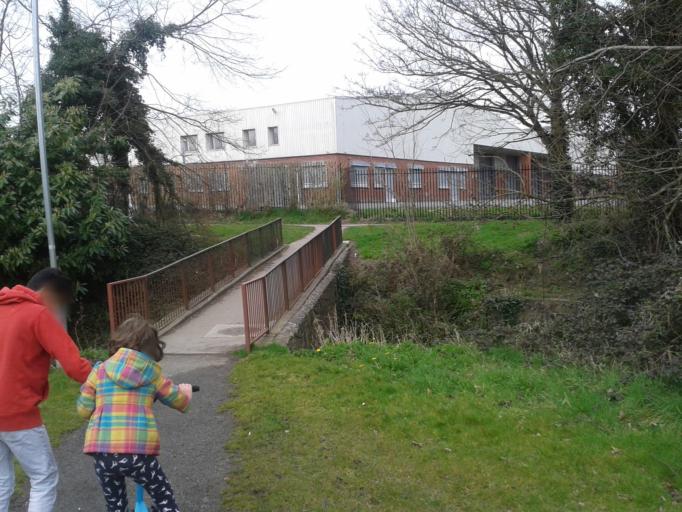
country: IE
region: Leinster
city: Beaumont
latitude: 53.4036
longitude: -6.2385
